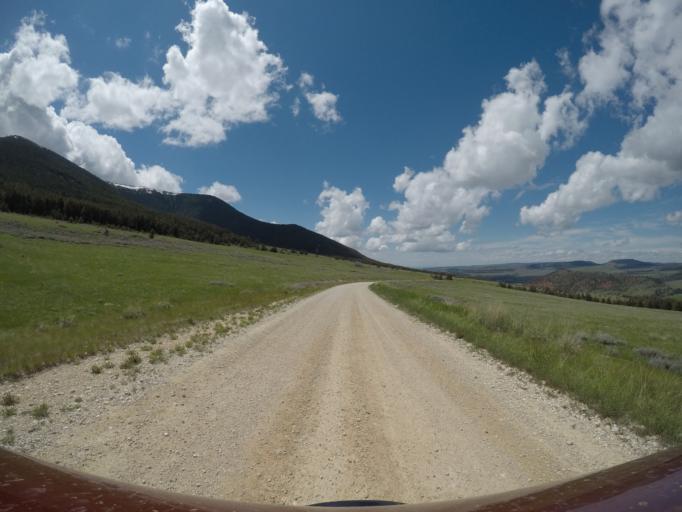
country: US
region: Wyoming
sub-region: Big Horn County
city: Lovell
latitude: 45.1879
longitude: -108.4704
